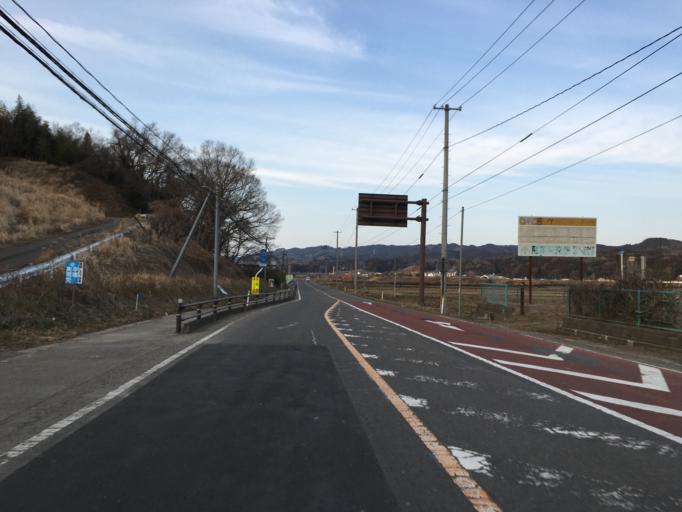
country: JP
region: Ibaraki
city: Daigo
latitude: 36.8627
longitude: 140.4148
